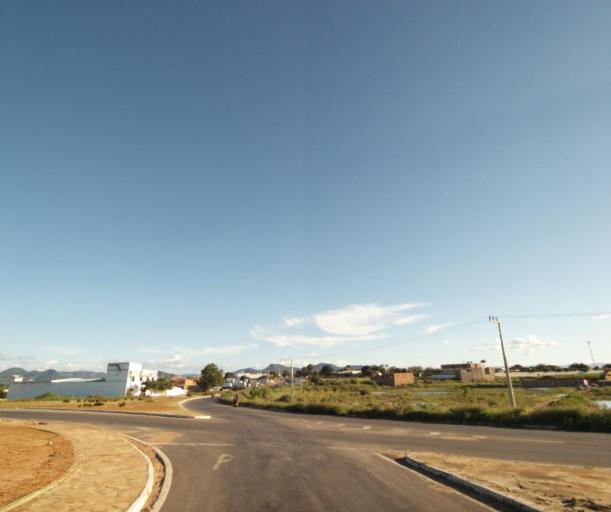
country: BR
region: Bahia
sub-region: Guanambi
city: Guanambi
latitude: -14.2091
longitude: -42.7651
